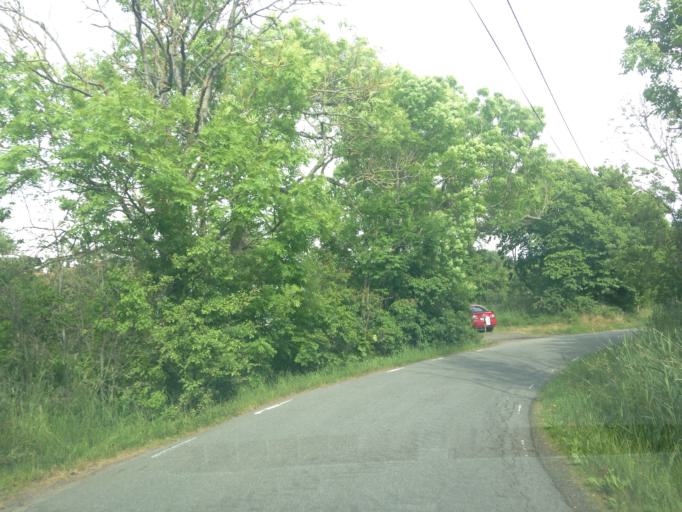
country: SE
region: Vaestra Goetaland
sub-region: Goteborg
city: Majorna
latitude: 57.7563
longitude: 11.8660
